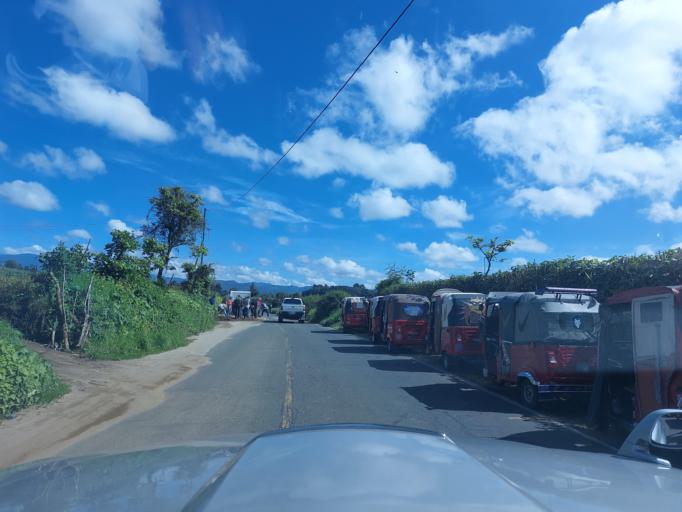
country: GT
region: Chimaltenango
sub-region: Municipio de Zaragoza
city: Zaragoza
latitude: 14.6608
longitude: -90.8979
